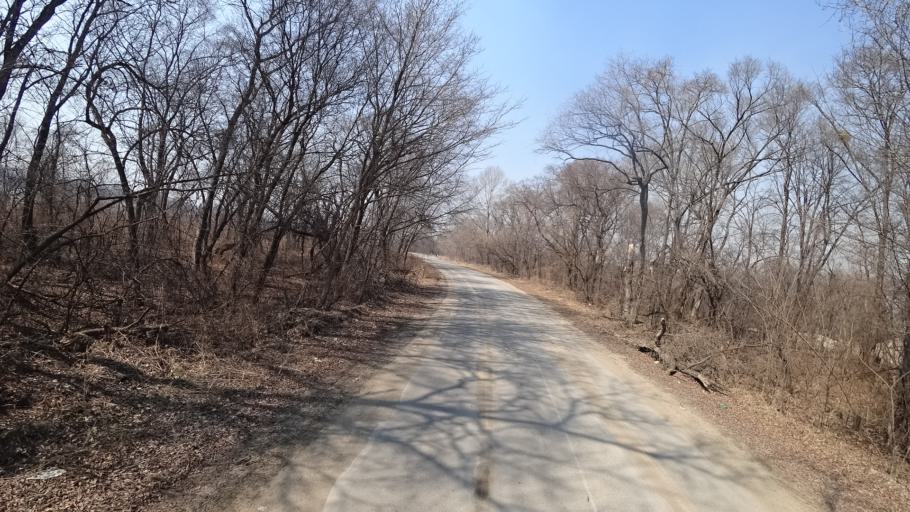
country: RU
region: Amur
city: Novobureyskiy
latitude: 49.7900
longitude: 129.9069
